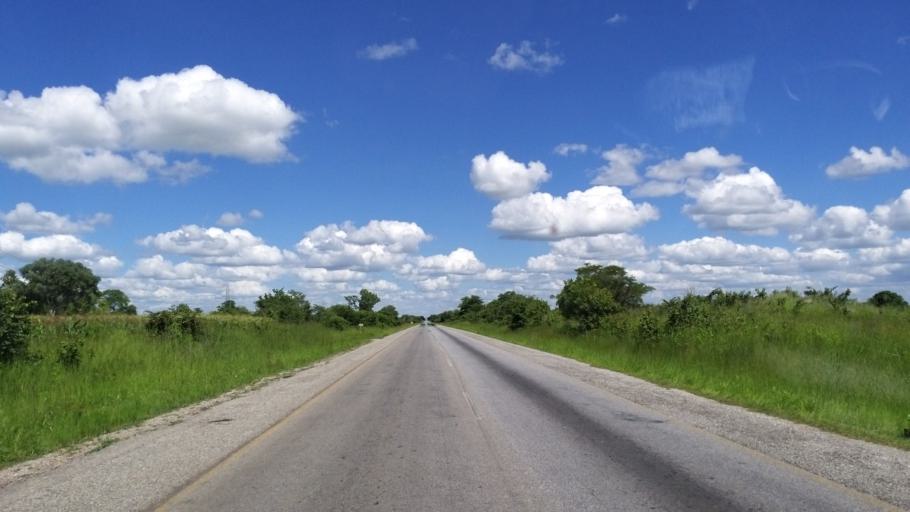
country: ZM
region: Central
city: Mumbwa
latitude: -15.2071
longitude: 27.6062
